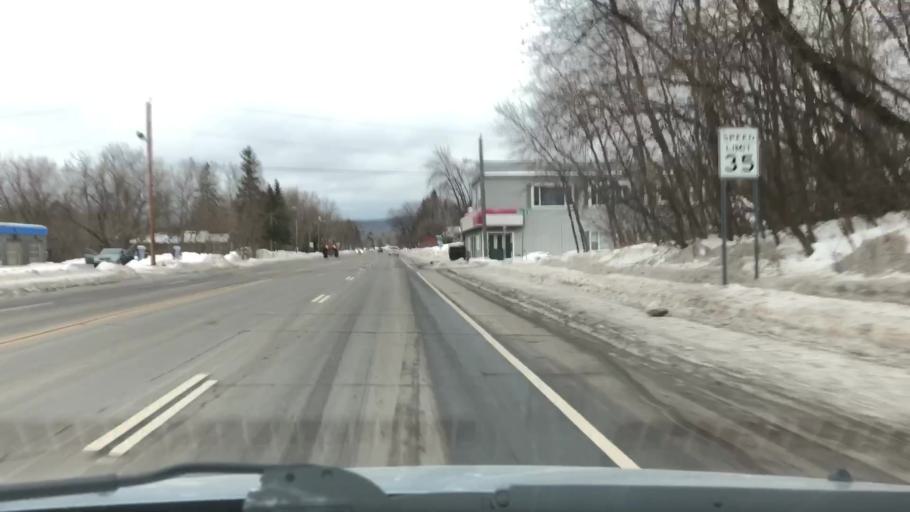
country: US
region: Minnesota
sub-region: Saint Louis County
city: Proctor
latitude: 46.7217
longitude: -92.1936
